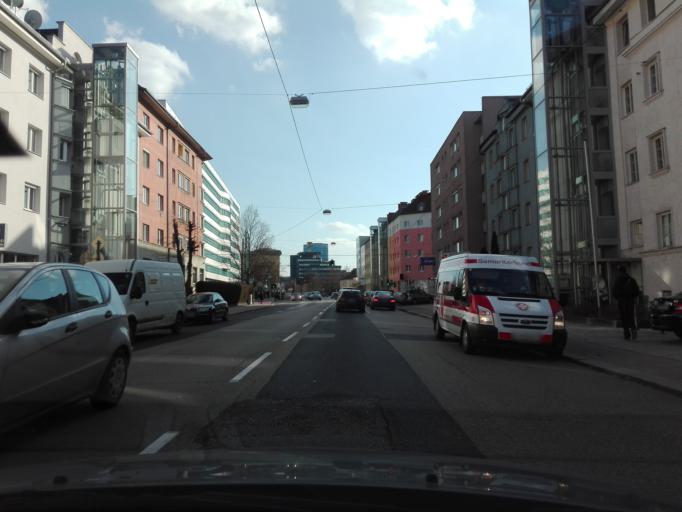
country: AT
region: Upper Austria
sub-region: Linz Stadt
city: Linz
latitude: 48.3043
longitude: 14.3003
